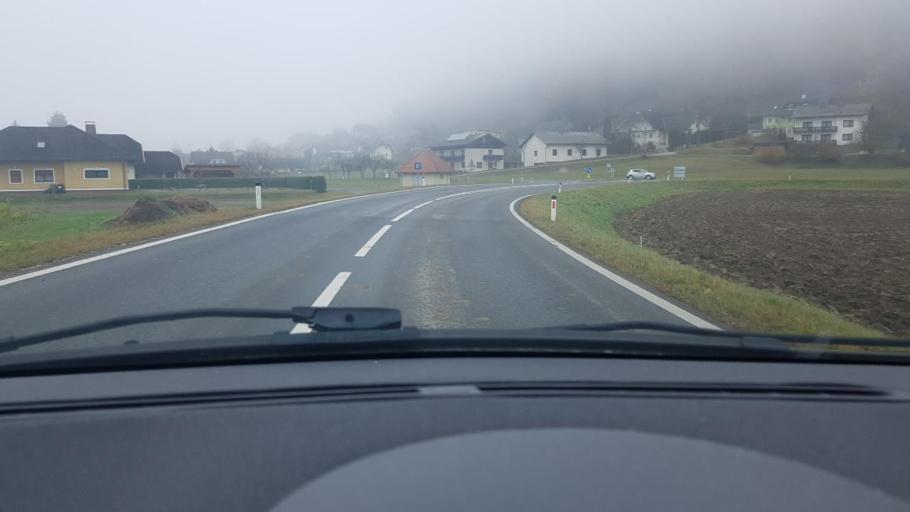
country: AT
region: Carinthia
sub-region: Politischer Bezirk Volkermarkt
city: Sittersdorf
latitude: 46.5488
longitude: 14.6087
